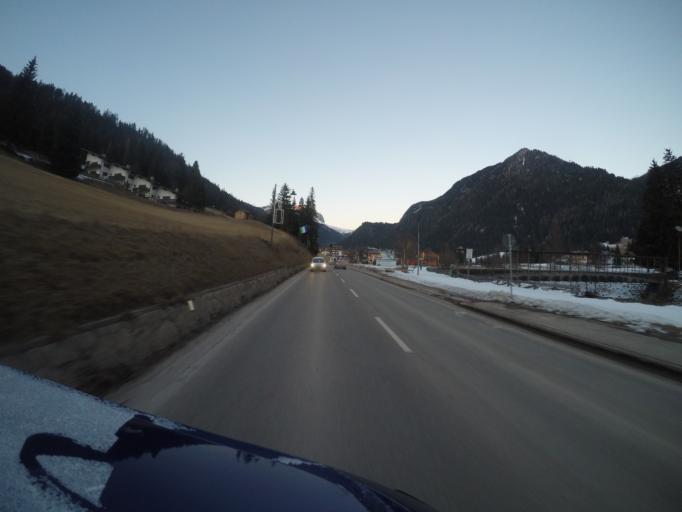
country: IT
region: Trentino-Alto Adige
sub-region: Provincia di Trento
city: Pozza di Fassa
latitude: 46.4319
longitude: 11.6865
